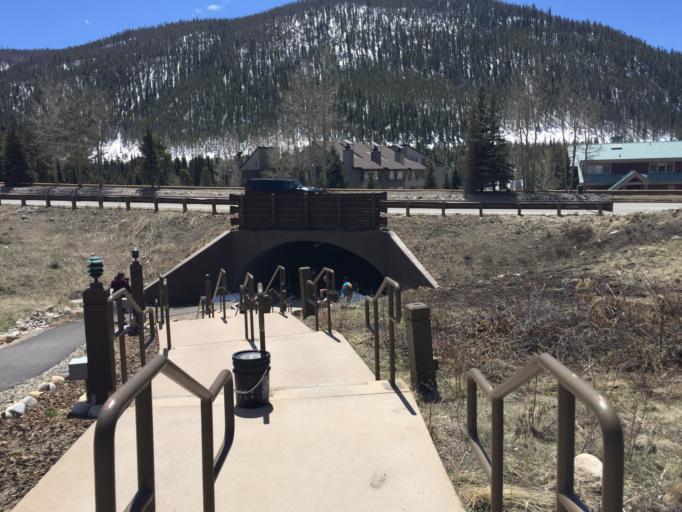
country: US
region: Colorado
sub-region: Summit County
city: Keystone
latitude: 39.6082
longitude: -105.9671
